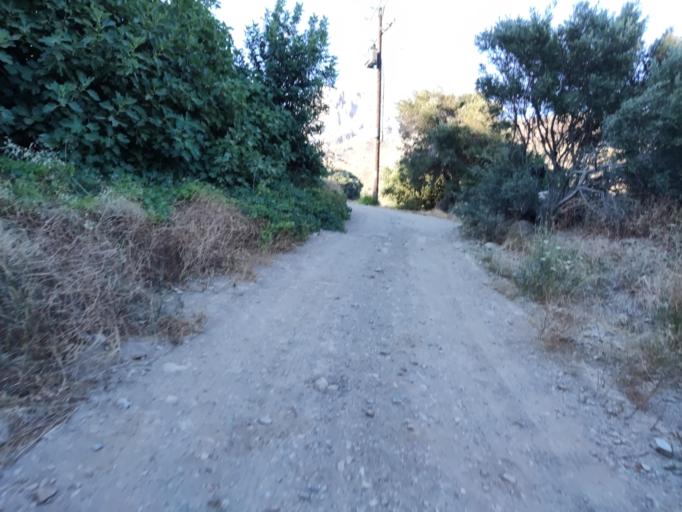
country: GR
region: Crete
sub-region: Nomos Rethymnis
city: Atsipopoulon
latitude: 35.2006
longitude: 24.3933
